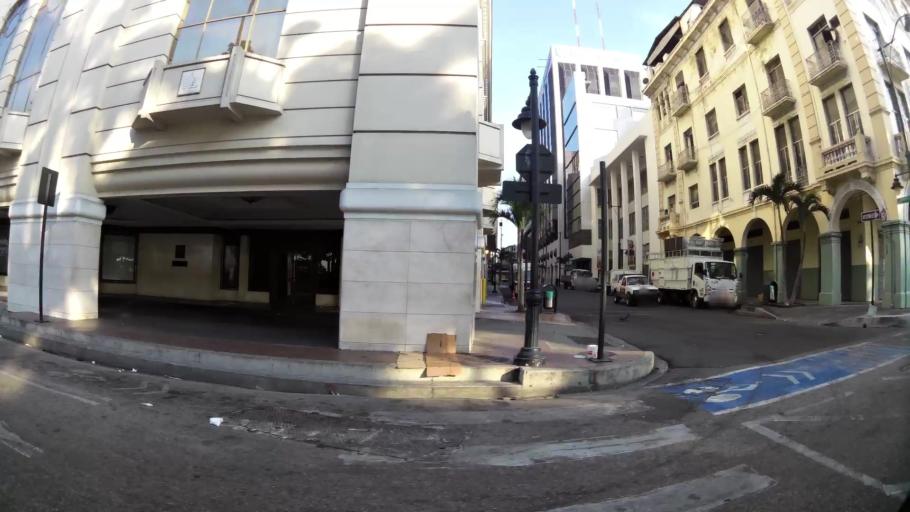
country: EC
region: Guayas
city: Eloy Alfaro
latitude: -2.1918
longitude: -79.8795
